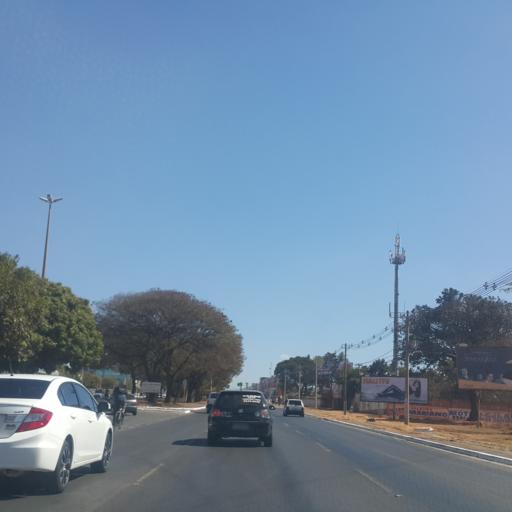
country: BR
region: Federal District
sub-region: Brasilia
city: Brasilia
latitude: -15.8120
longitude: -48.0945
